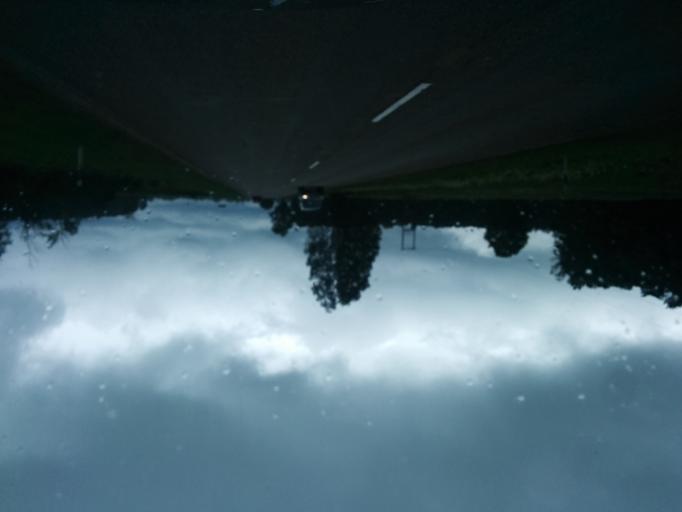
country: LV
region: Beverina
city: Murmuiza
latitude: 57.4911
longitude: 25.5719
